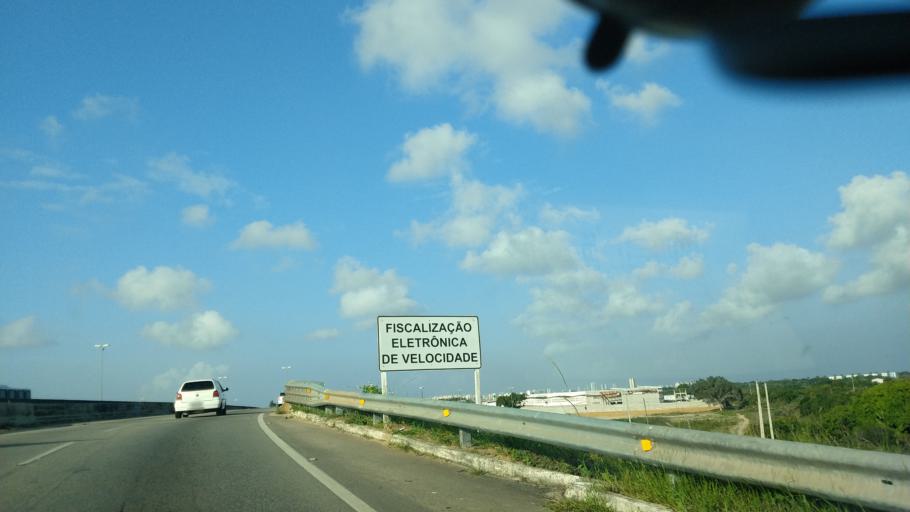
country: BR
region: Rio Grande do Norte
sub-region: Parnamirim
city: Parnamirim
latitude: -5.8923
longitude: -35.2567
